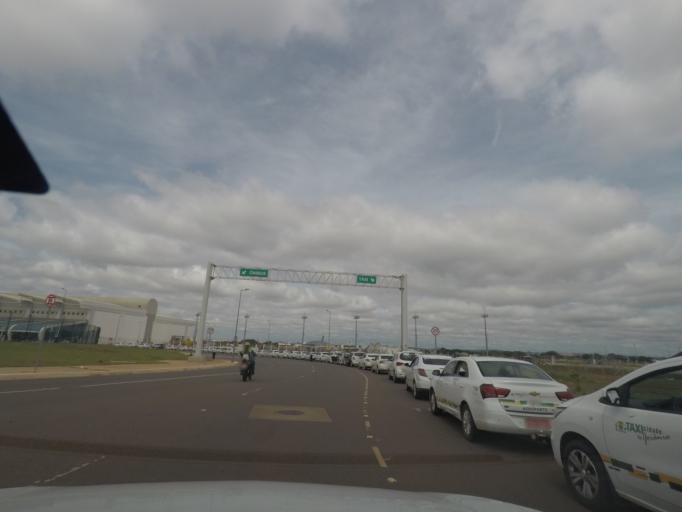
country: BR
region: Goias
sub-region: Goiania
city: Goiania
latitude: -16.6276
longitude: -49.2135
